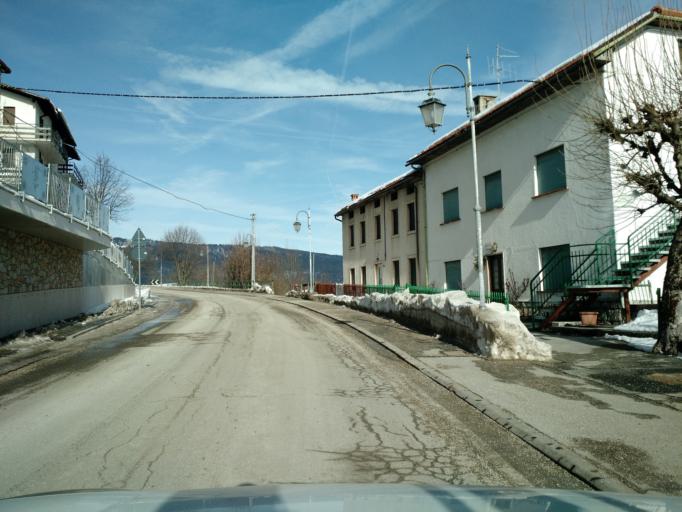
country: IT
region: Veneto
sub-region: Provincia di Vicenza
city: Canove di Roana
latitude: 45.8399
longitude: 11.4533
